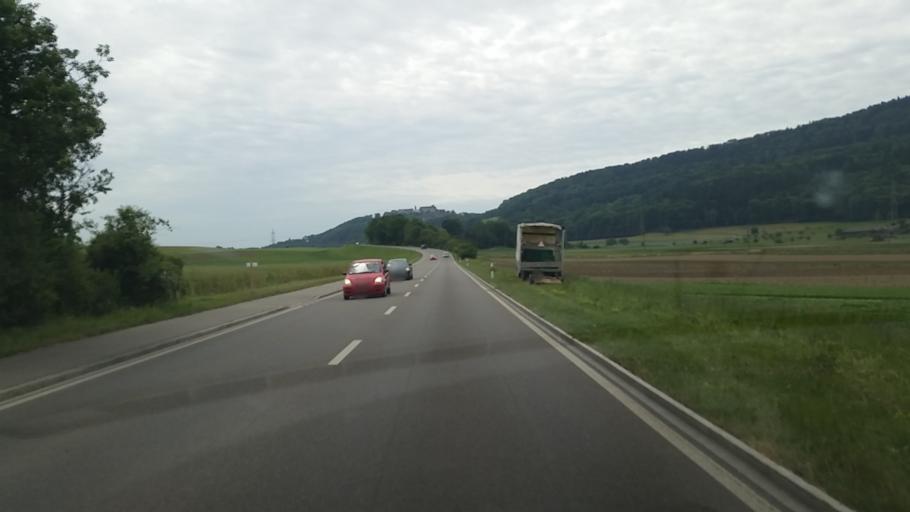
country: CH
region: Zurich
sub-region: Bezirk Dielsdorf
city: Steinmaur
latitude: 47.4979
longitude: 8.4206
